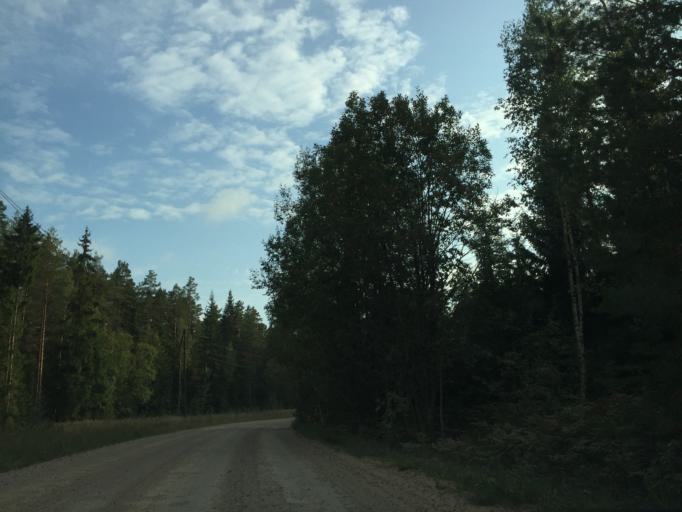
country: LV
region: Ikskile
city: Ikskile
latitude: 56.8031
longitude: 24.4404
